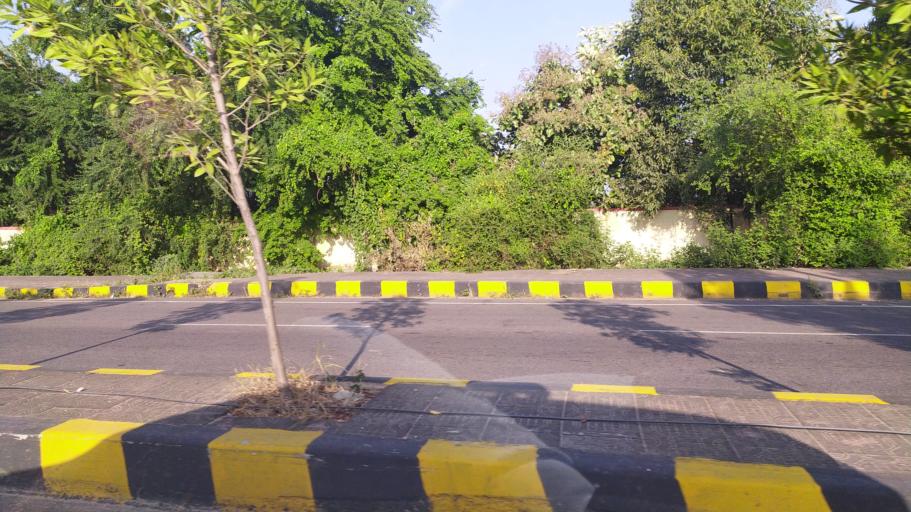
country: IN
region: Telangana
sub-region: Hyderabad
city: Hyderabad
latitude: 17.3243
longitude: 78.4062
